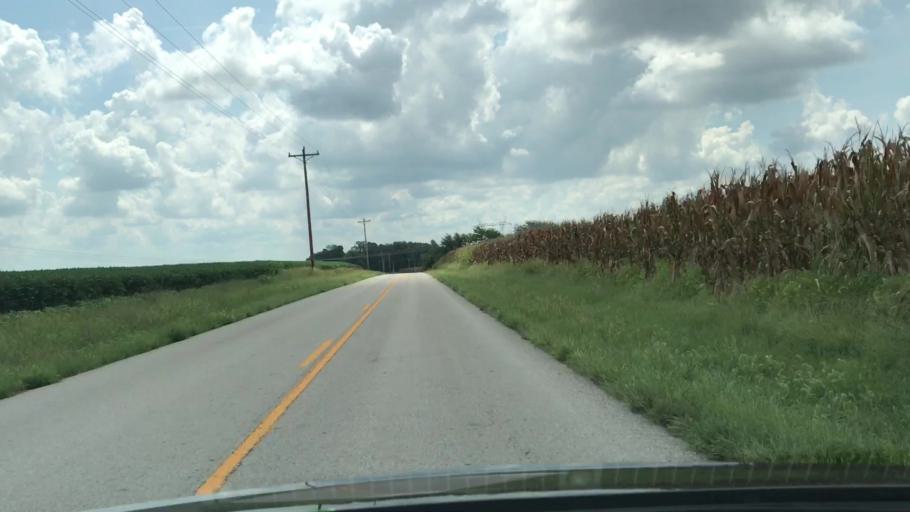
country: US
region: Kentucky
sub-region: Todd County
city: Elkton
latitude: 36.7765
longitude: -87.1193
